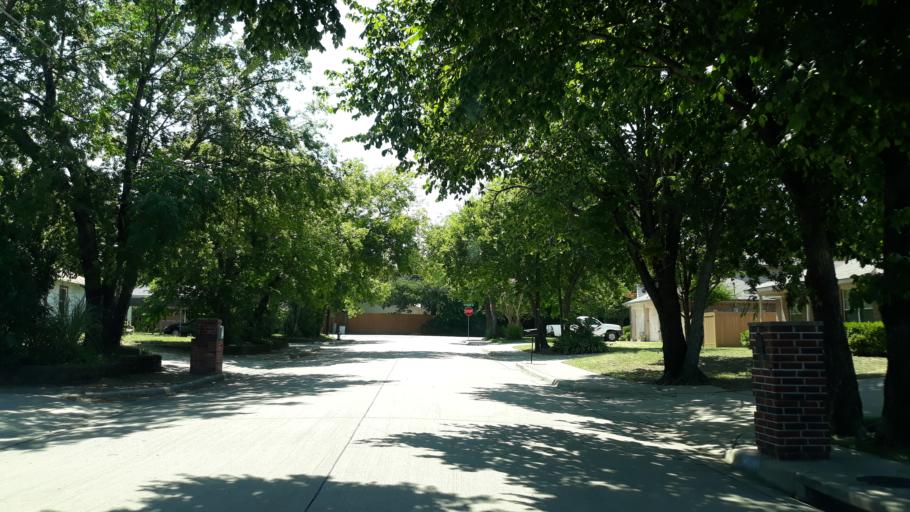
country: US
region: Texas
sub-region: Dallas County
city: Irving
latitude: 32.8252
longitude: -97.0036
